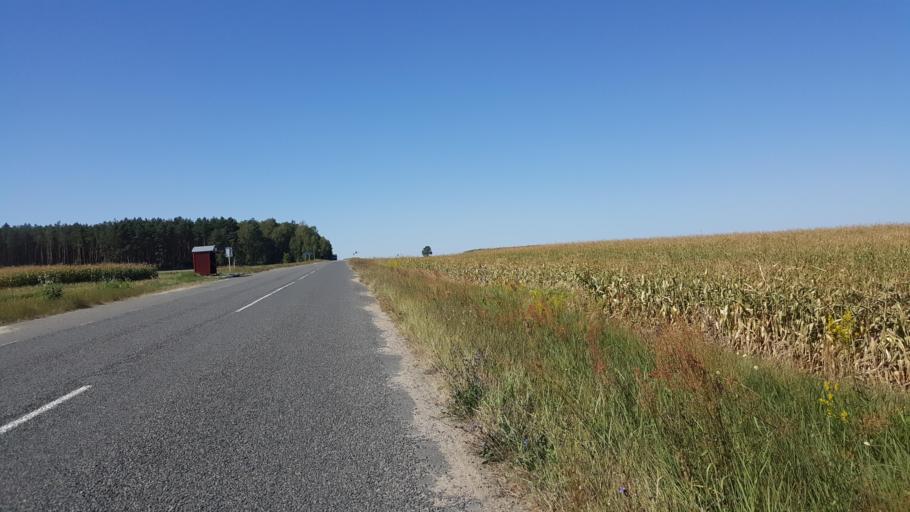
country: PL
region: Lublin Voivodeship
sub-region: Powiat bialski
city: Rokitno
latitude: 52.2223
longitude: 23.4012
